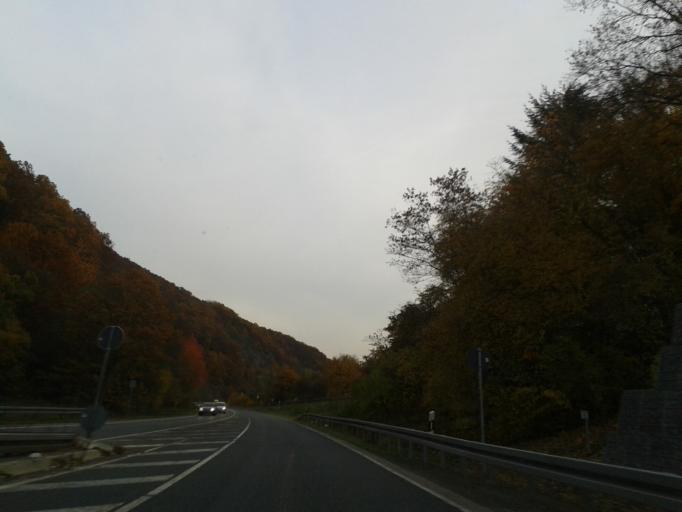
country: DE
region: Hesse
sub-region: Regierungsbezirk Giessen
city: Sinn
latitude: 50.6661
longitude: 8.3212
